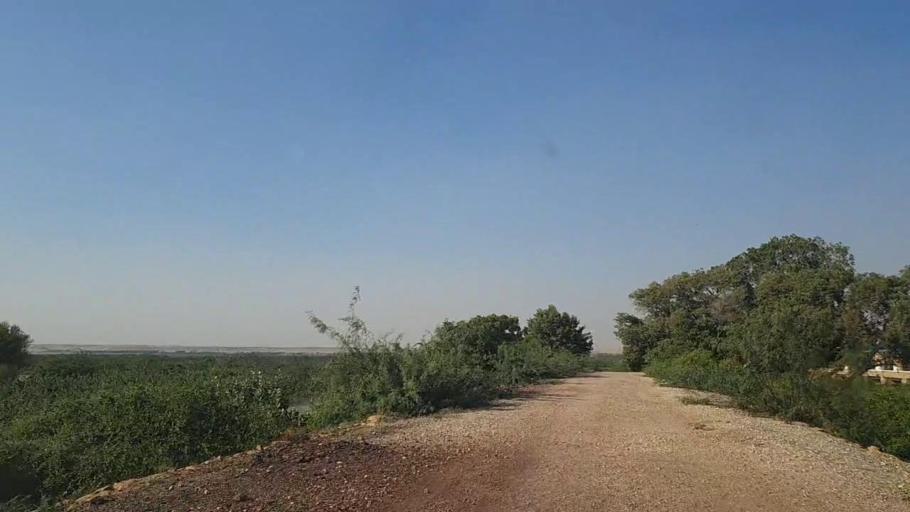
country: PK
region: Sindh
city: Daro Mehar
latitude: 25.0379
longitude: 68.1362
